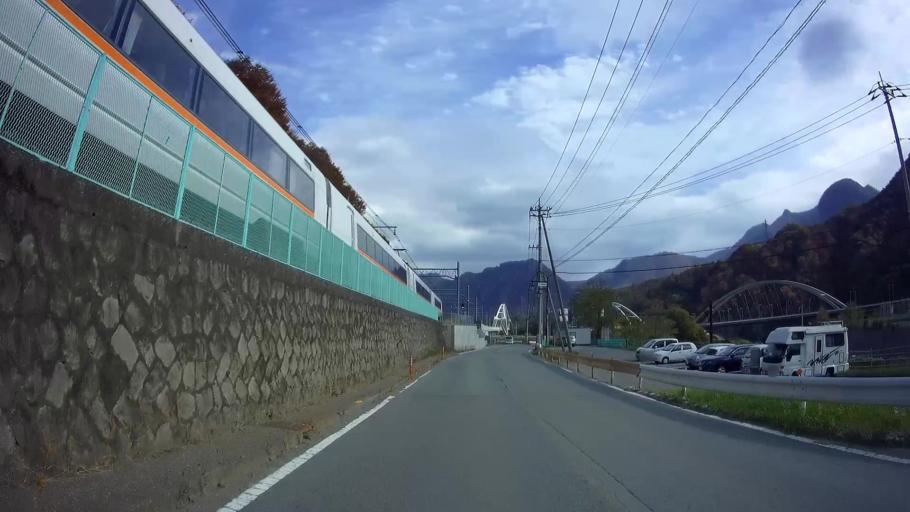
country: JP
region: Gunma
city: Nakanojomachi
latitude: 36.5460
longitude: 138.6499
